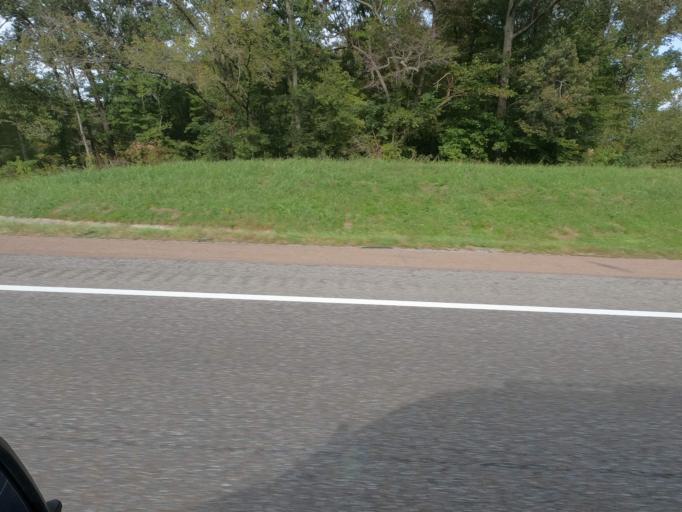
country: US
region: Tennessee
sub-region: Henderson County
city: Lexington
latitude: 35.7853
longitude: -88.4052
